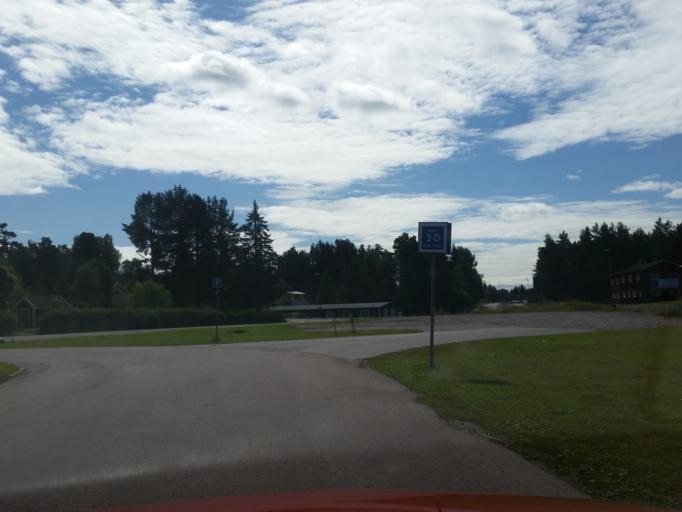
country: SE
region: Dalarna
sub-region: Leksand Municipality
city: Smedby
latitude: 60.6730
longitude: 15.0890
